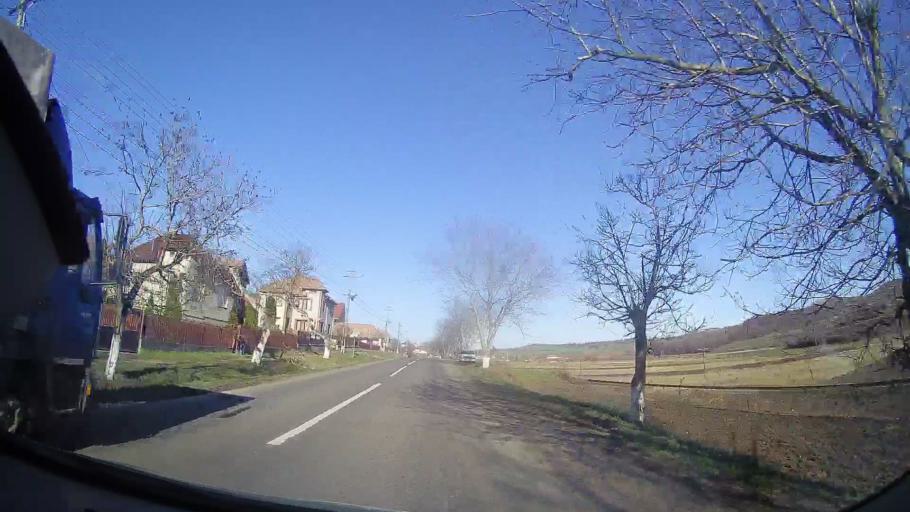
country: RO
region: Mures
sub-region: Comuna Sarmasu
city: Balda
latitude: 46.7252
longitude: 24.1435
